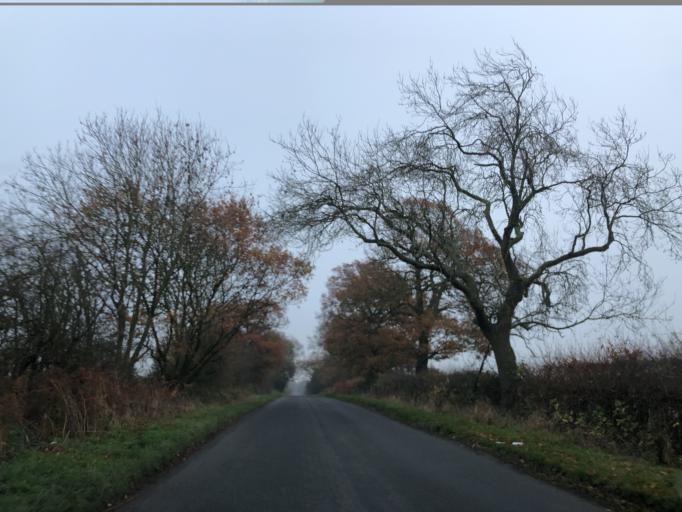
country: GB
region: England
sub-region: Solihull
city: Balsall Common
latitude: 52.3680
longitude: -1.6546
